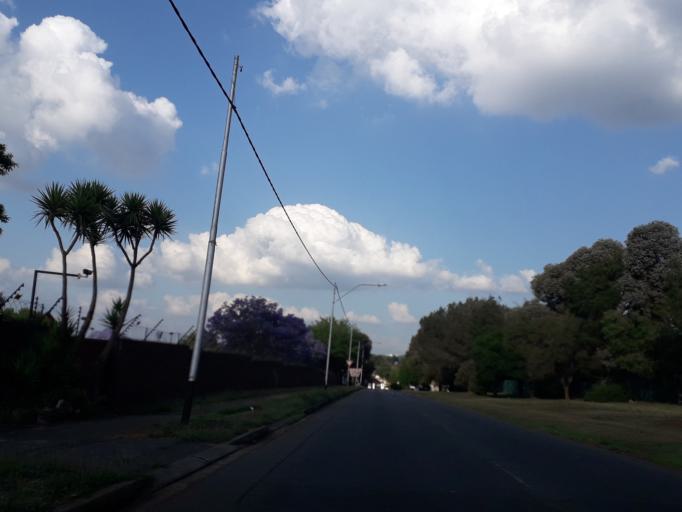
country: ZA
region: Gauteng
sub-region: City of Johannesburg Metropolitan Municipality
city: Johannesburg
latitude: -26.1516
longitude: 27.9995
